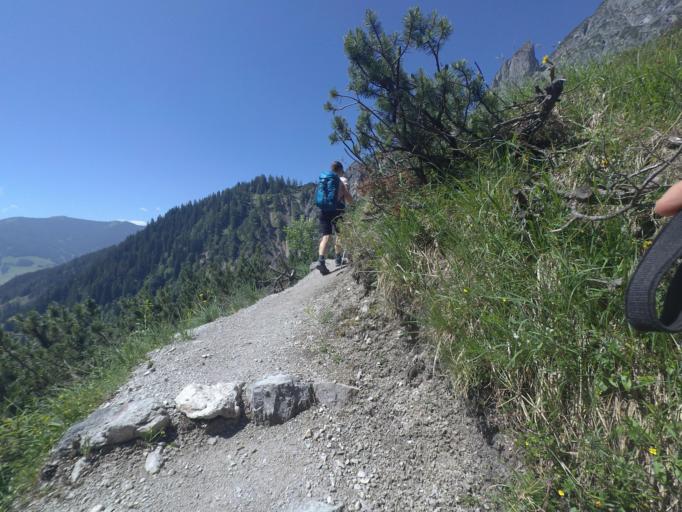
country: AT
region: Salzburg
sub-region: Politischer Bezirk Zell am See
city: Leogang
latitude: 47.4656
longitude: 12.7460
